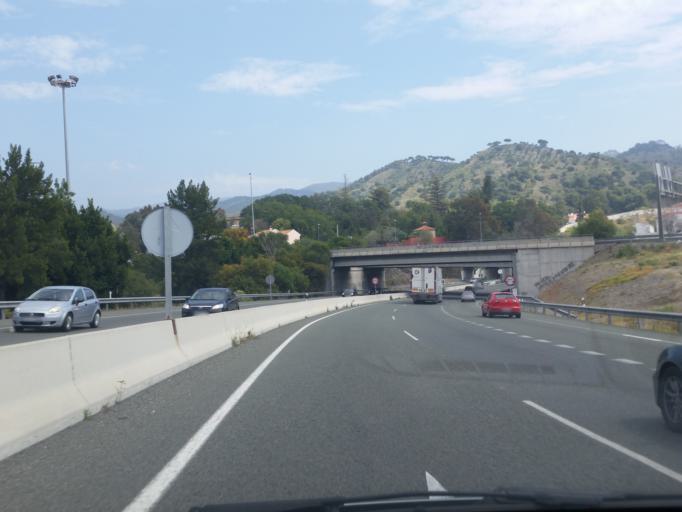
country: ES
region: Andalusia
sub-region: Provincia de Malaga
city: Malaga
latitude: 36.7567
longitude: -4.4277
